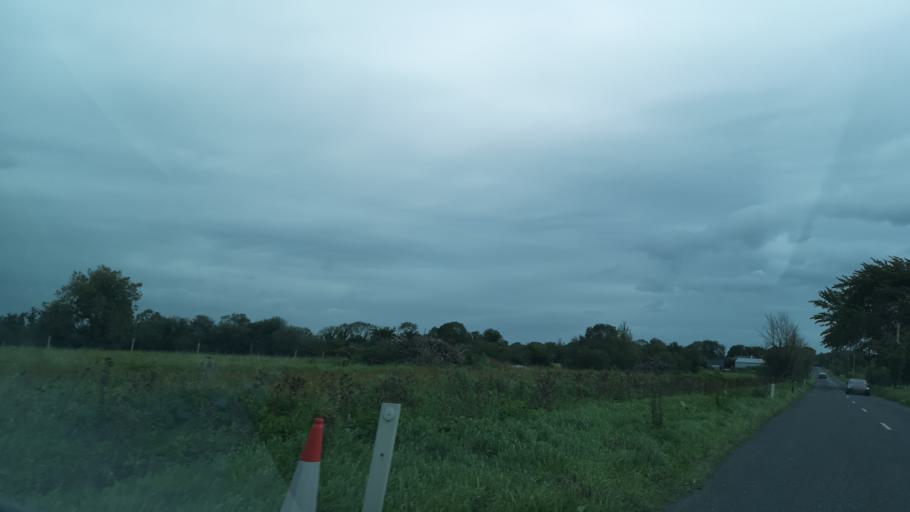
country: IE
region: Leinster
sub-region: Uibh Fhaili
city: Banagher
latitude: 53.2031
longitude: -7.9479
